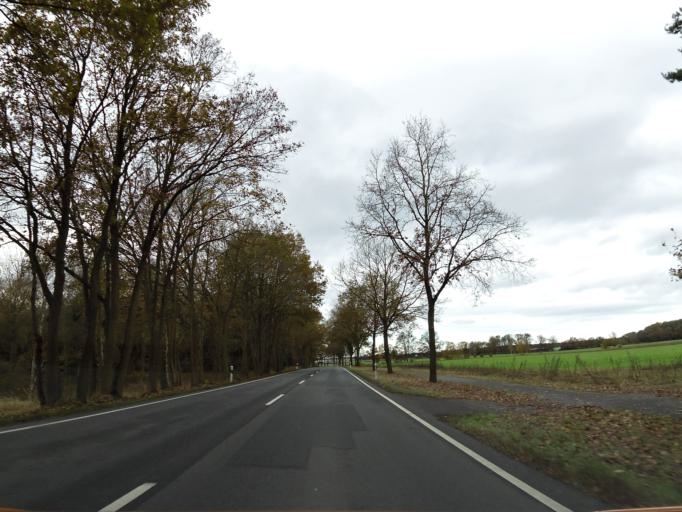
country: DE
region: Lower Saxony
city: Suderburg
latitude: 52.9521
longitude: 10.4973
